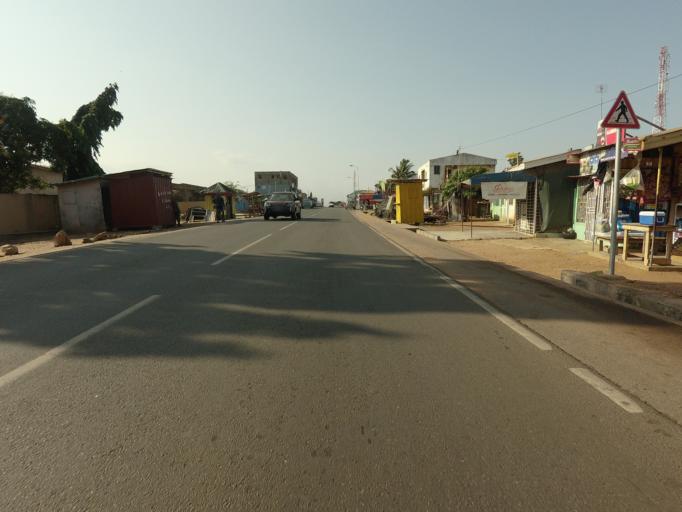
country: GH
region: Greater Accra
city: Nungua
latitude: 5.6299
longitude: -0.0763
